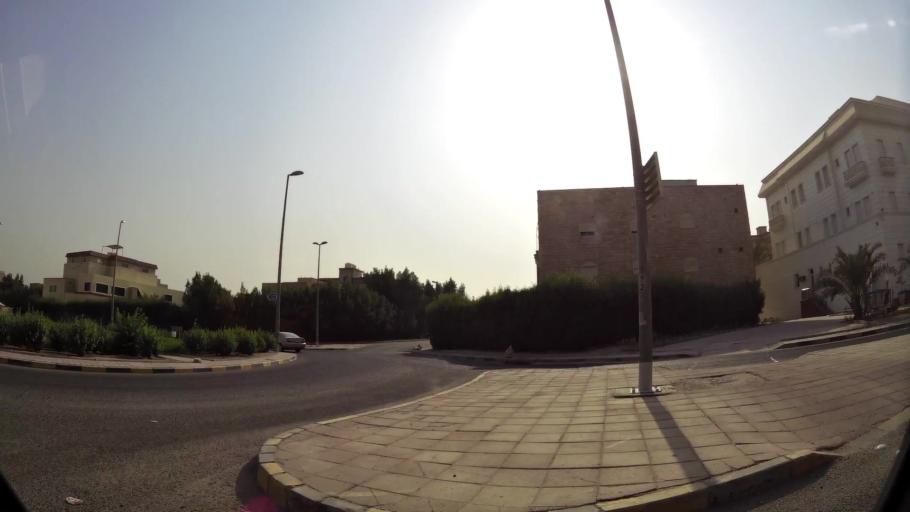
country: KW
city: Al Funaytis
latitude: 29.2202
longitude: 48.0814
